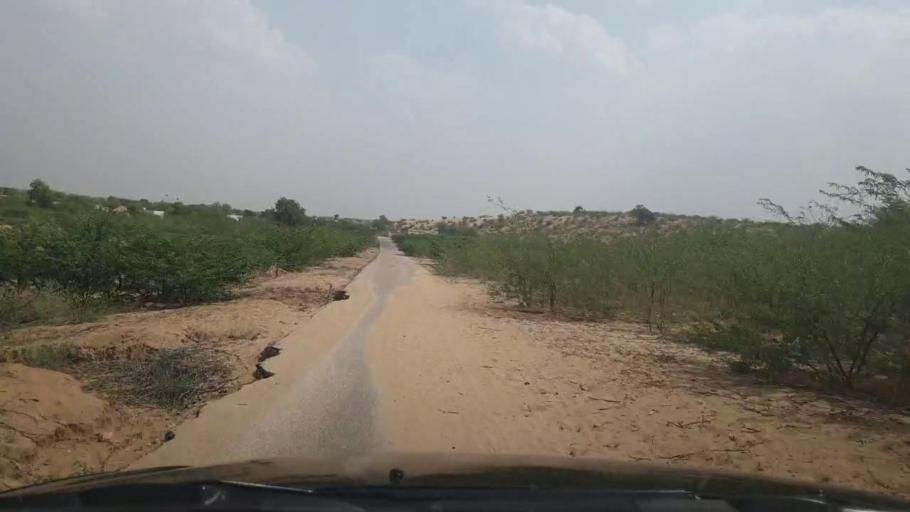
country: PK
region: Sindh
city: Islamkot
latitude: 25.0293
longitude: 70.5457
